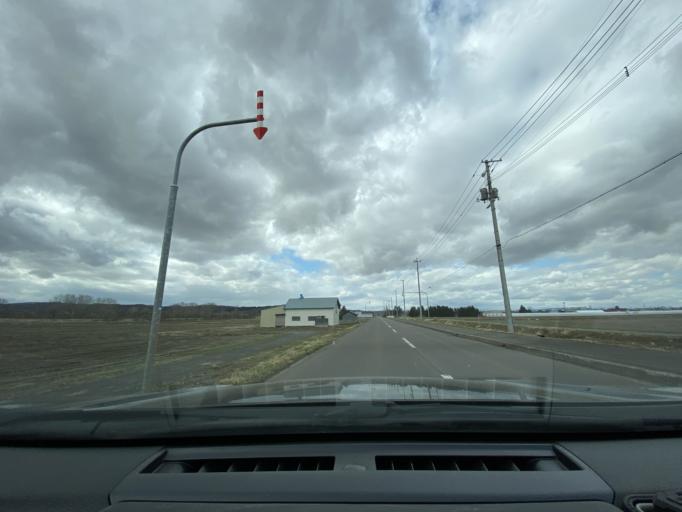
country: JP
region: Hokkaido
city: Nayoro
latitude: 44.1299
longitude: 142.4920
